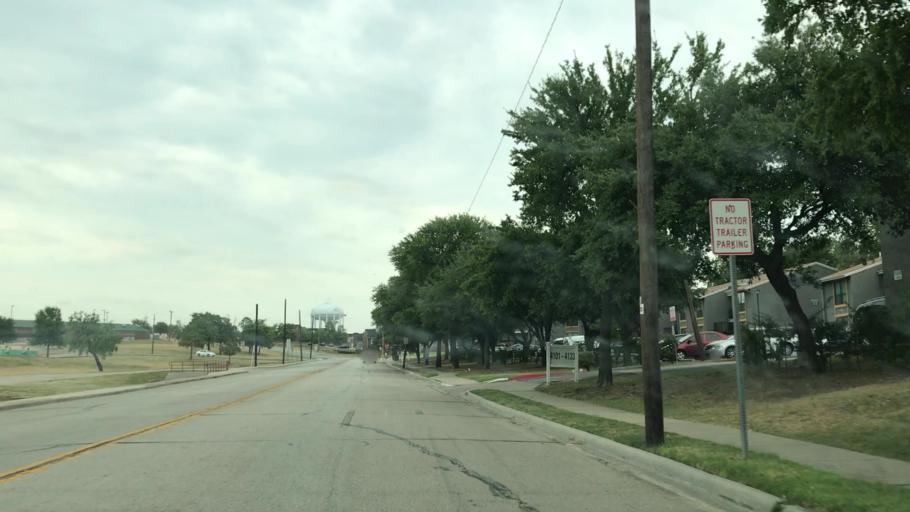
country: US
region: Texas
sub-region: Dallas County
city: Irving
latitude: 32.8620
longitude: -96.9886
